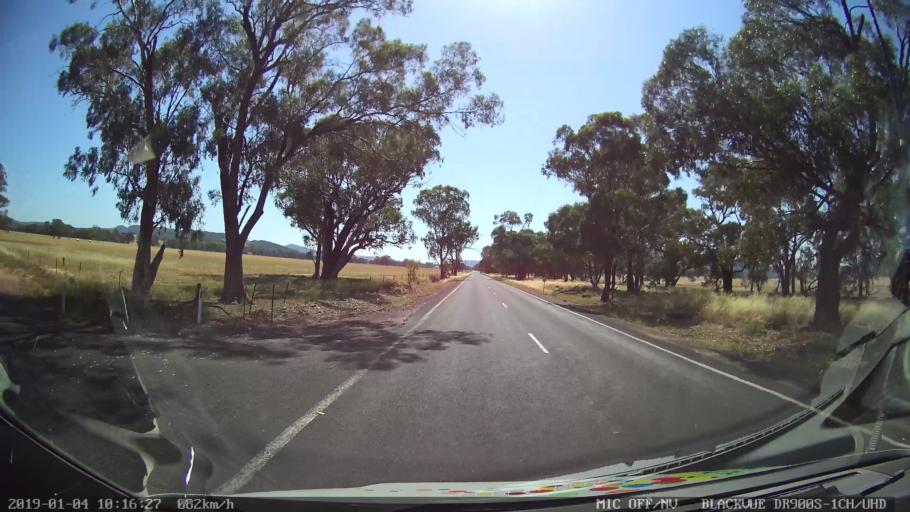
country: AU
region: New South Wales
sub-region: Cabonne
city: Canowindra
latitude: -33.3854
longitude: 148.4370
